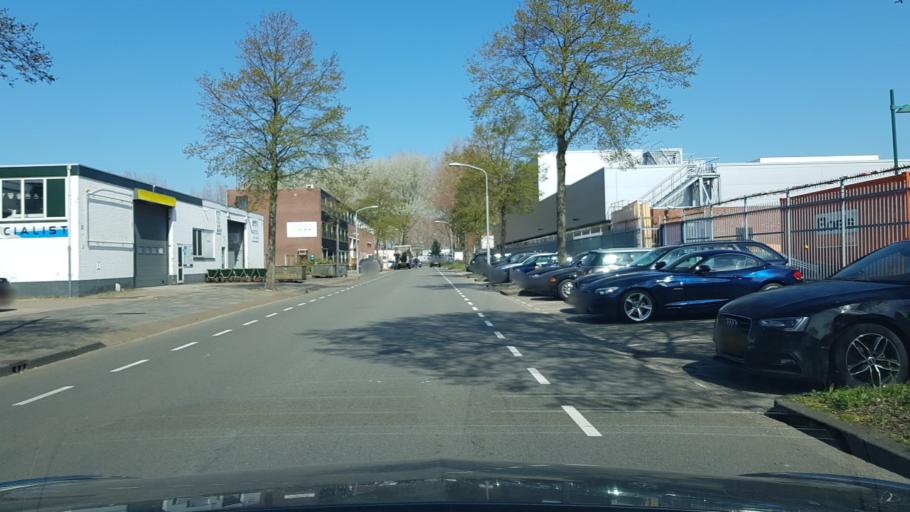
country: NL
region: North Holland
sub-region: Gemeente Haarlem
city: Haarlem
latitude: 52.3896
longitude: 4.6582
